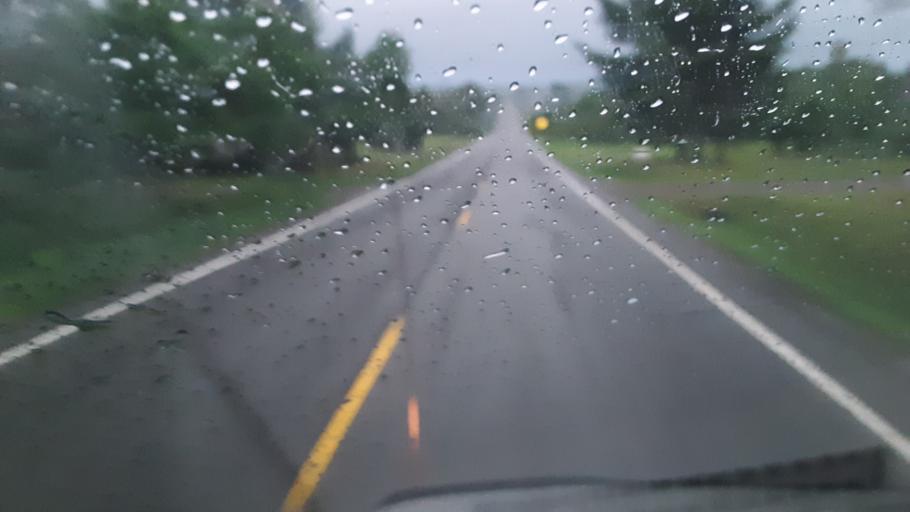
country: US
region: Maine
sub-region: Penobscot County
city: Patten
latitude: 46.0110
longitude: -68.4463
